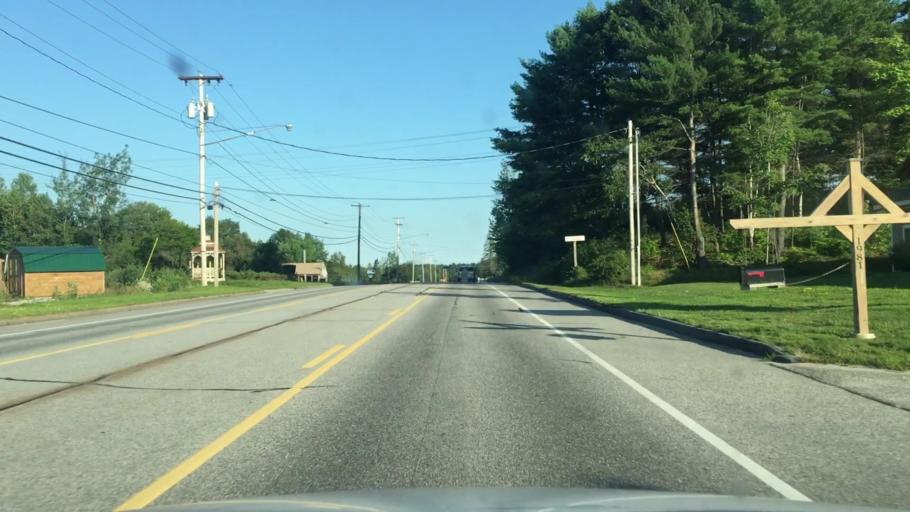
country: US
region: Maine
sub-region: Androscoggin County
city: Lisbon
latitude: 44.0592
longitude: -70.1450
